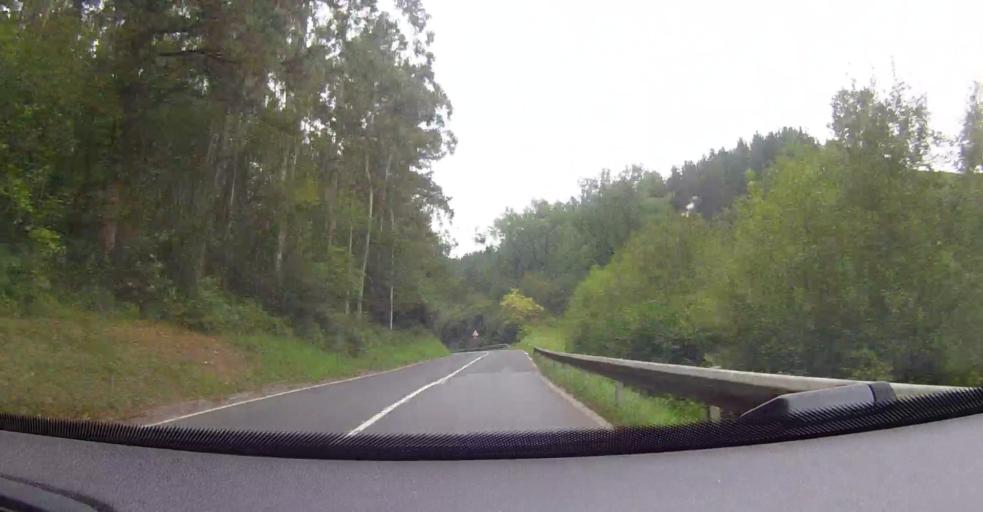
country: ES
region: Basque Country
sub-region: Bizkaia
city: Balmaseda
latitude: 43.2410
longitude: -3.2278
